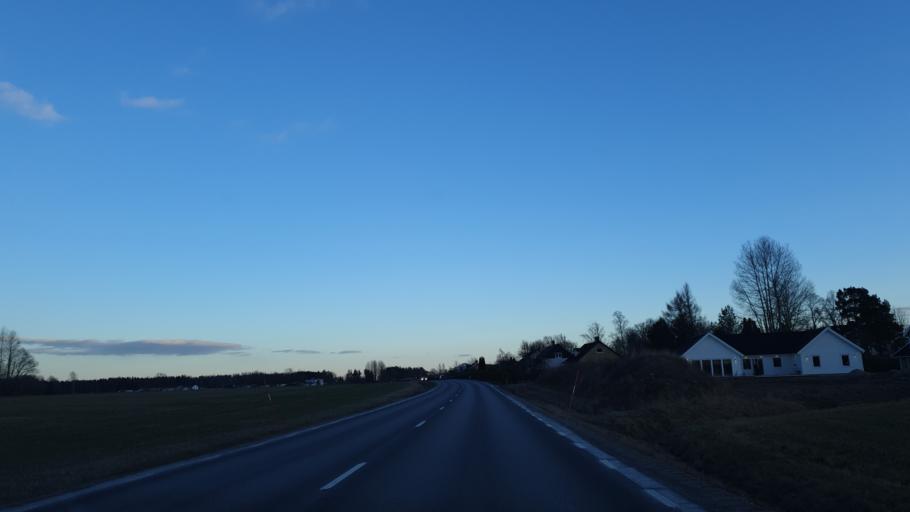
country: SE
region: OErebro
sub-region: Orebro Kommun
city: Orebro
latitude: 59.3100
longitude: 15.1479
